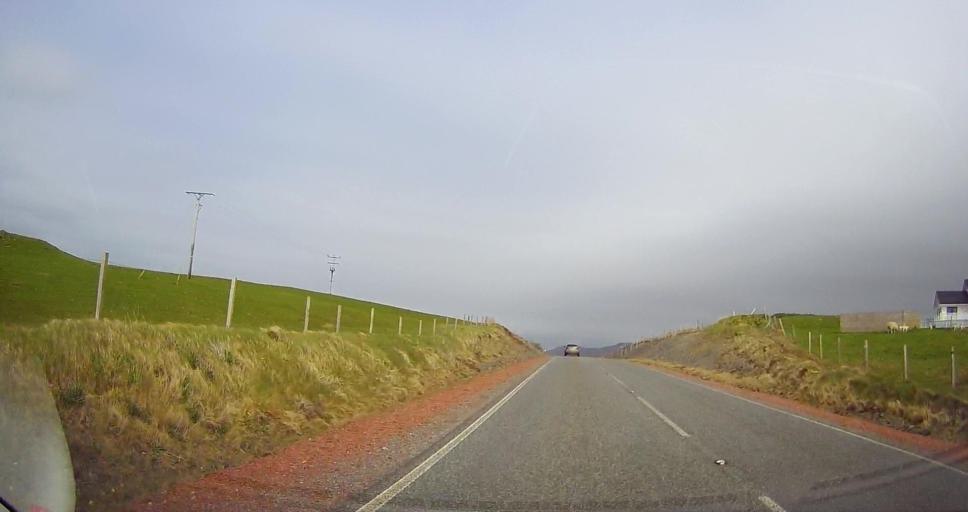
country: GB
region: Scotland
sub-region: Shetland Islands
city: Sandwick
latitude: 60.1198
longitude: -1.2896
